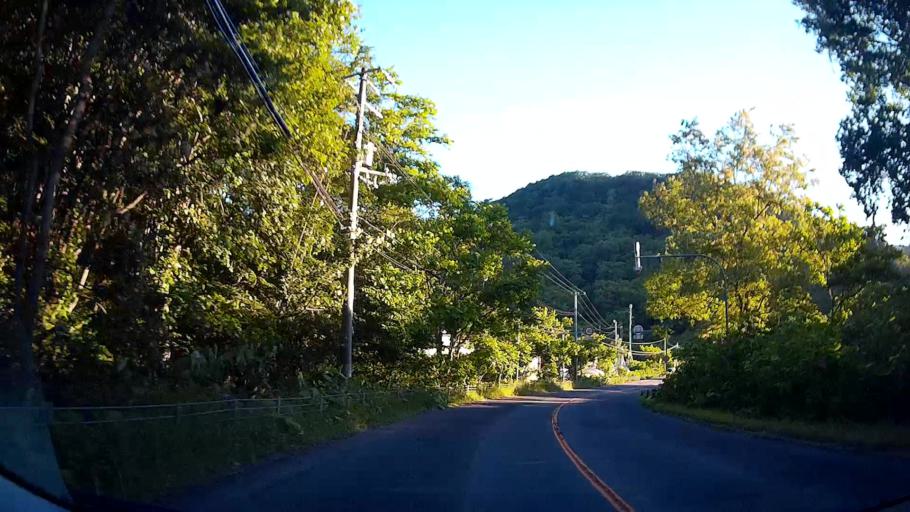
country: JP
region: Hokkaido
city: Otaru
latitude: 43.1624
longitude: 141.0005
